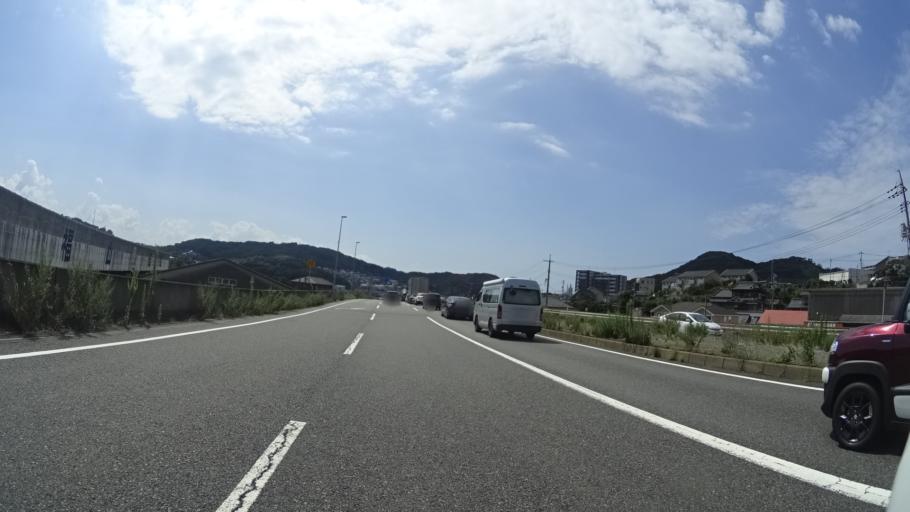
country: JP
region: Yamaguchi
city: Shimonoseki
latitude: 33.9812
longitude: 130.9499
